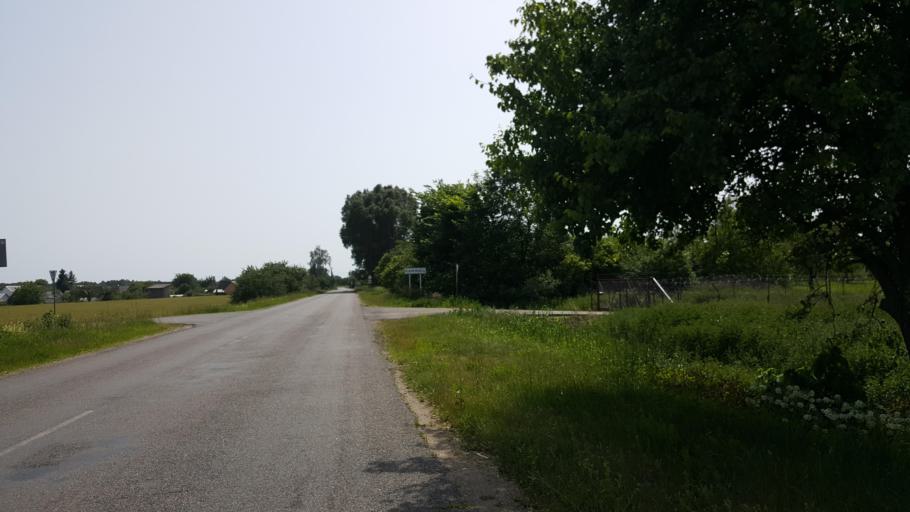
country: BY
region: Brest
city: Kamyanyets
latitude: 52.4103
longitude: 23.7985
